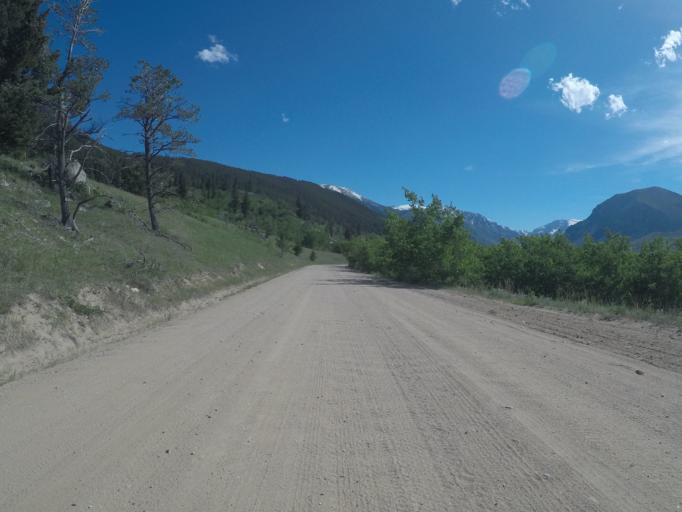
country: US
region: Montana
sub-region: Stillwater County
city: Absarokee
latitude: 45.2954
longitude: -109.5350
